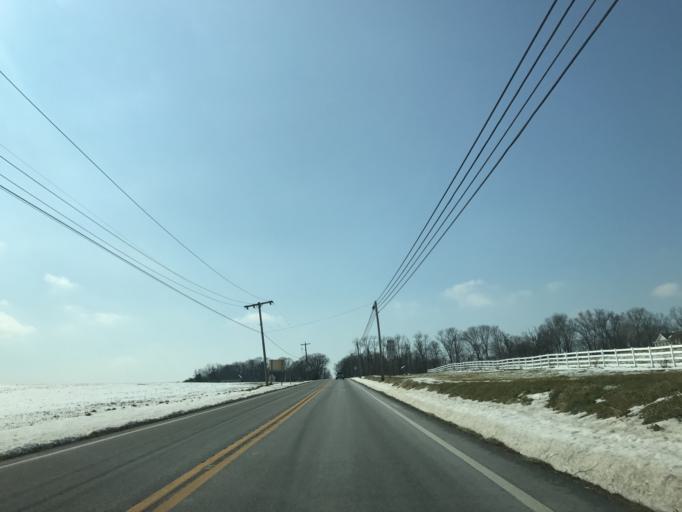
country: US
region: Maryland
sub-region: Harford County
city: Jarrettsville
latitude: 39.6971
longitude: -76.4511
